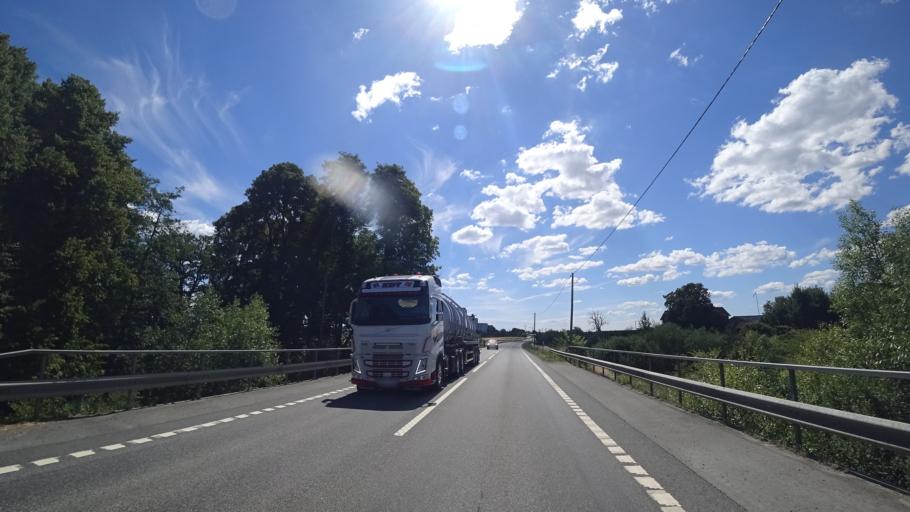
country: SE
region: Skane
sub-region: Kristianstads Kommun
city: Kristianstad
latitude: 56.0447
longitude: 14.0890
